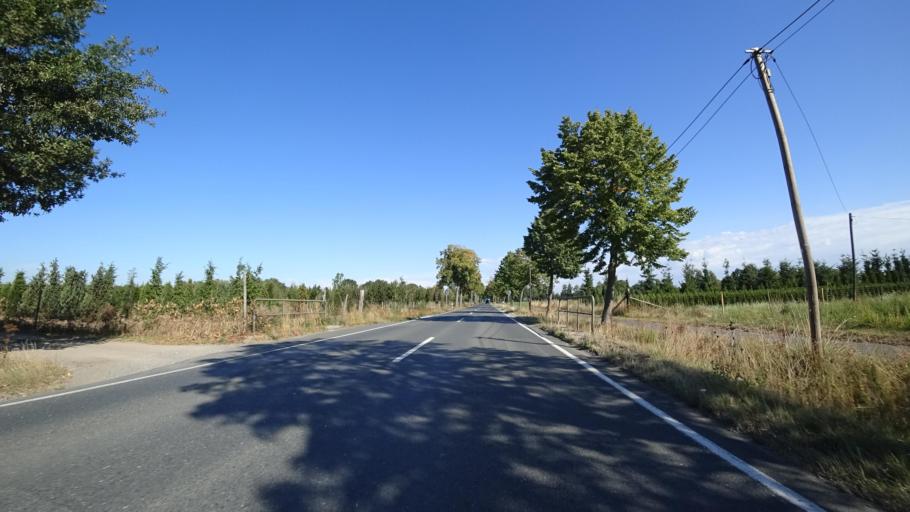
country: DE
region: North Rhine-Westphalia
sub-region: Regierungsbezirk Detmold
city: Rheda-Wiedenbruck
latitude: 51.8850
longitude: 8.2812
